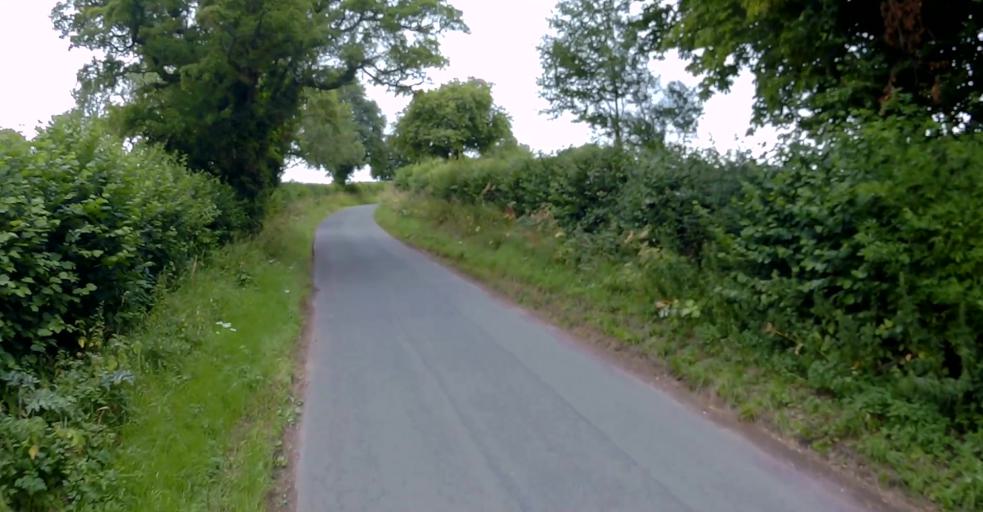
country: GB
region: England
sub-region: Hampshire
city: Kings Worthy
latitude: 51.0730
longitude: -1.2049
